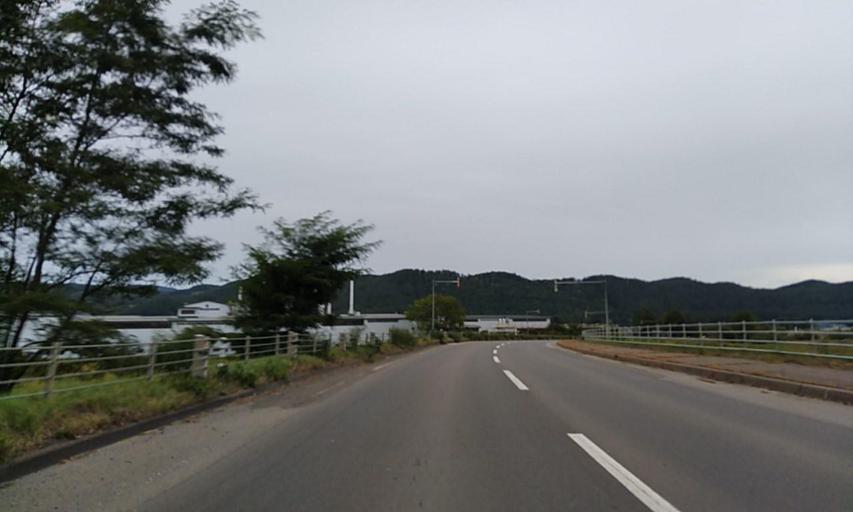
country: JP
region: Hokkaido
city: Bihoro
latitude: 43.7187
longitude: 144.0246
